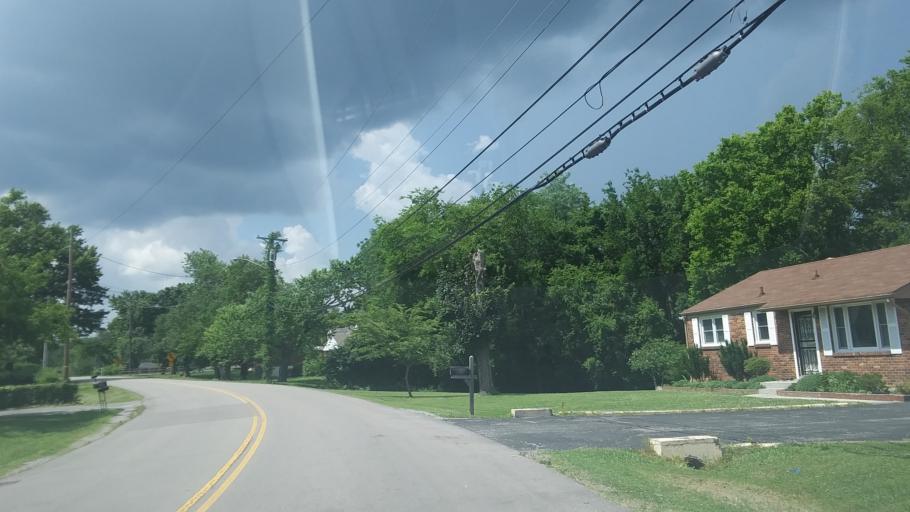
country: US
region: Tennessee
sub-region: Davidson County
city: Oak Hill
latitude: 36.0736
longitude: -86.7159
